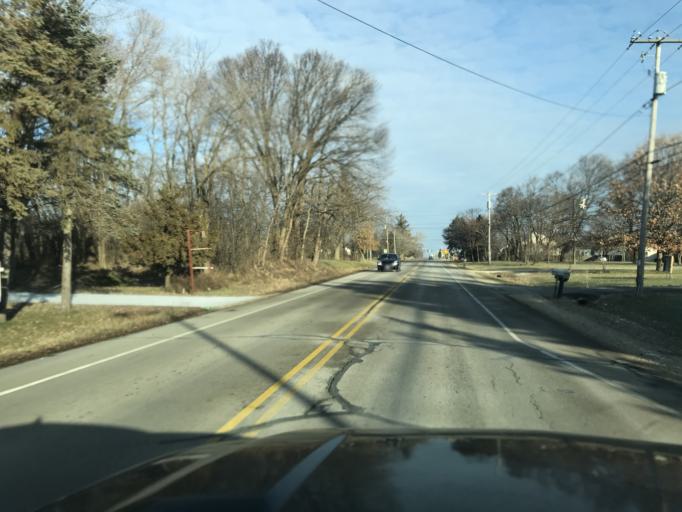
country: US
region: Wisconsin
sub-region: Kenosha County
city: Pleasant Prairie
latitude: 42.5726
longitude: -87.9143
